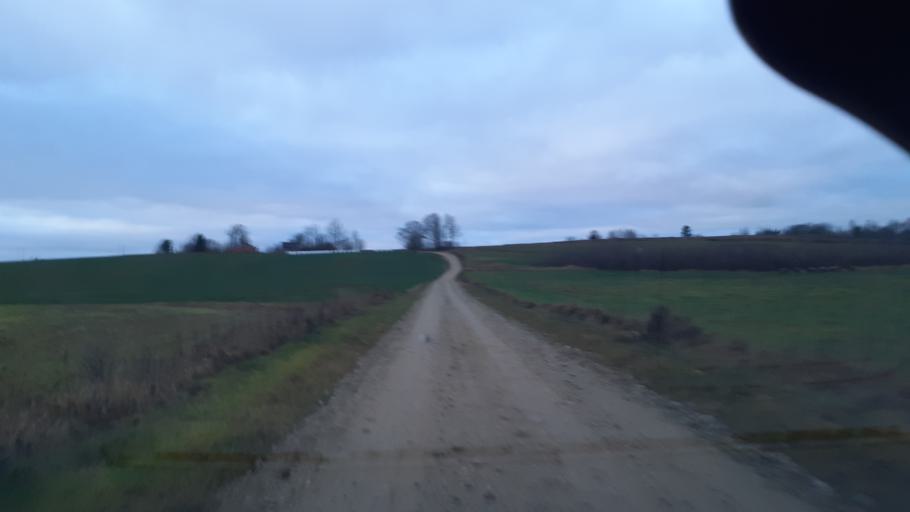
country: LV
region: Alsunga
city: Alsunga
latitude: 56.8954
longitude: 21.6288
